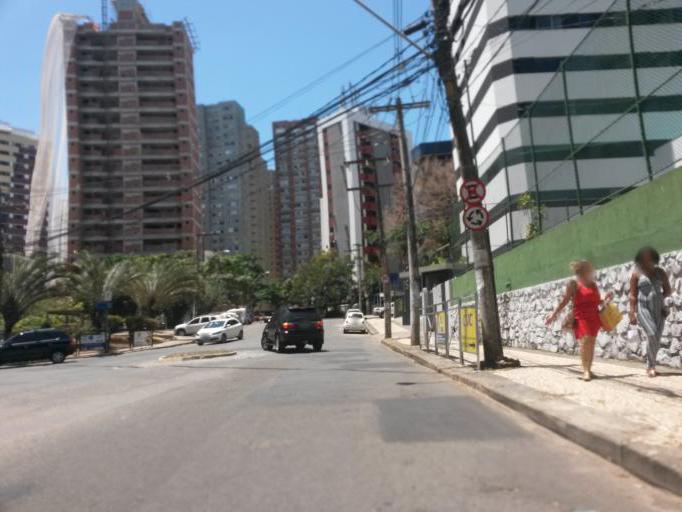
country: BR
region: Bahia
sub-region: Salvador
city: Salvador
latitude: -13.0035
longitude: -38.4621
